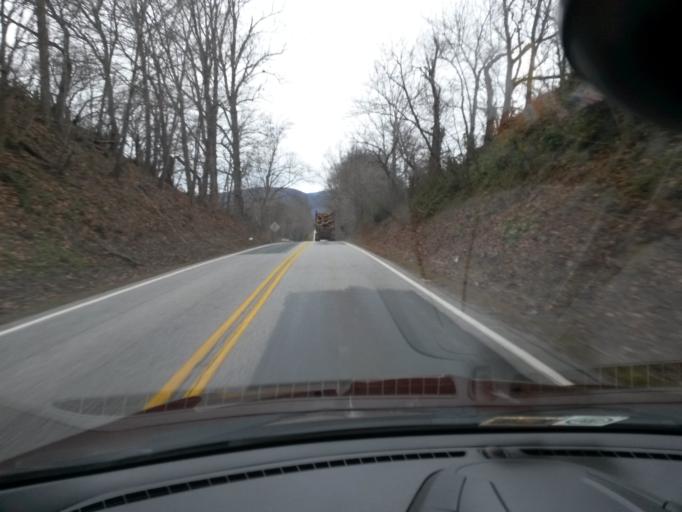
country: US
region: Virginia
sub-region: Amherst County
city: Amherst
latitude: 37.6519
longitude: -79.1350
